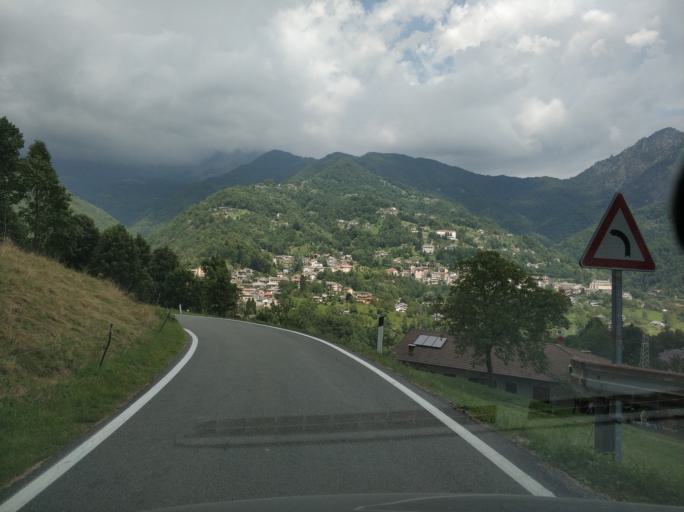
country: IT
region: Piedmont
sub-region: Provincia di Torino
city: Viu
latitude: 45.2288
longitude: 7.3752
